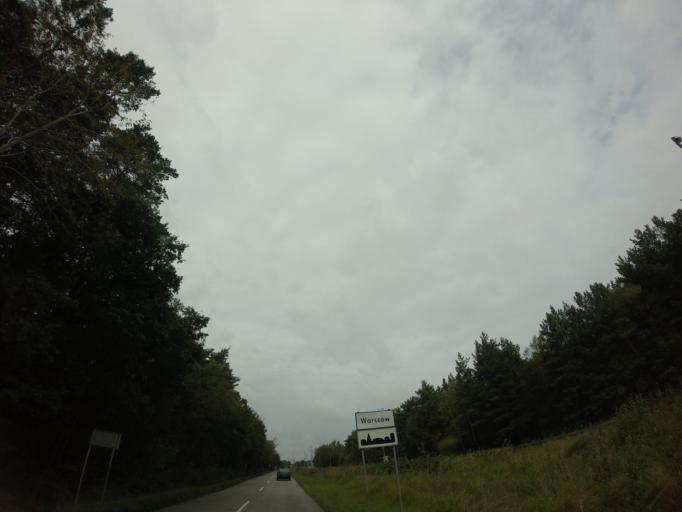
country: PL
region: West Pomeranian Voivodeship
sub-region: Swinoujscie
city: Swinoujscie
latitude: 53.9009
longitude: 14.2990
